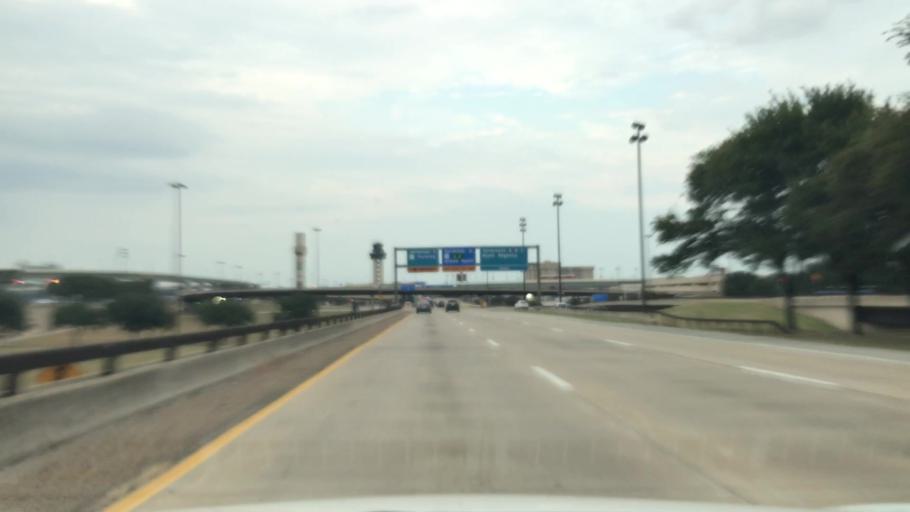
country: US
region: Texas
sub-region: Tarrant County
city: Grapevine
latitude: 32.8889
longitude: -97.0399
